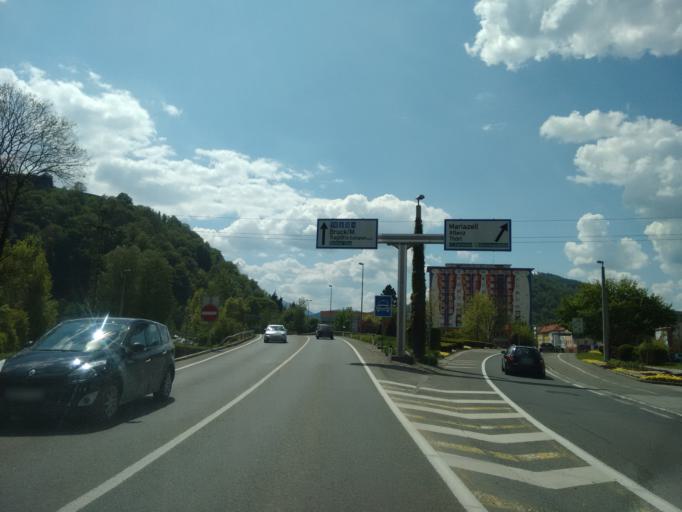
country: AT
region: Styria
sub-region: Politischer Bezirk Bruck-Muerzzuschlag
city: Kapfenberg
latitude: 47.4452
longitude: 15.2964
